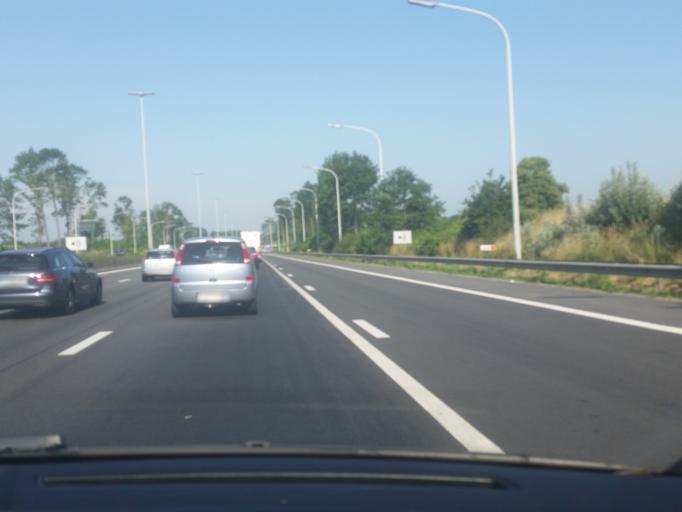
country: BE
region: Flanders
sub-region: Provincie Oost-Vlaanderen
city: Lede
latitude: 50.9289
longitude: 3.9510
